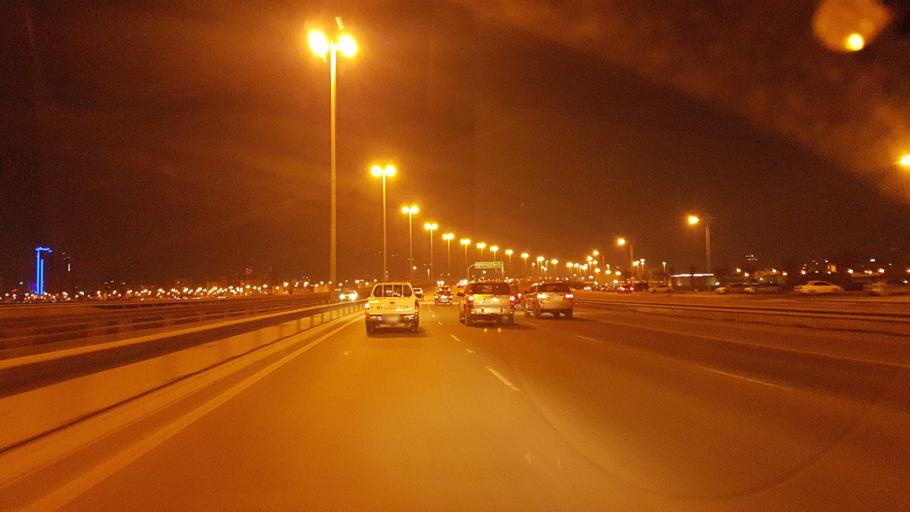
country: BH
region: Manama
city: Manama
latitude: 26.1900
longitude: 50.5888
